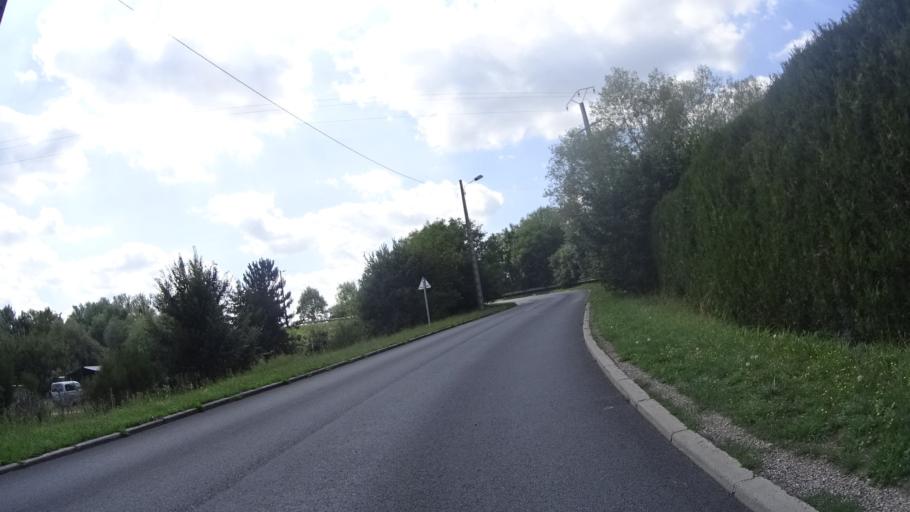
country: FR
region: Lorraine
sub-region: Departement de Meurthe-et-Moselle
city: Foug
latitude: 48.6797
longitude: 5.7902
